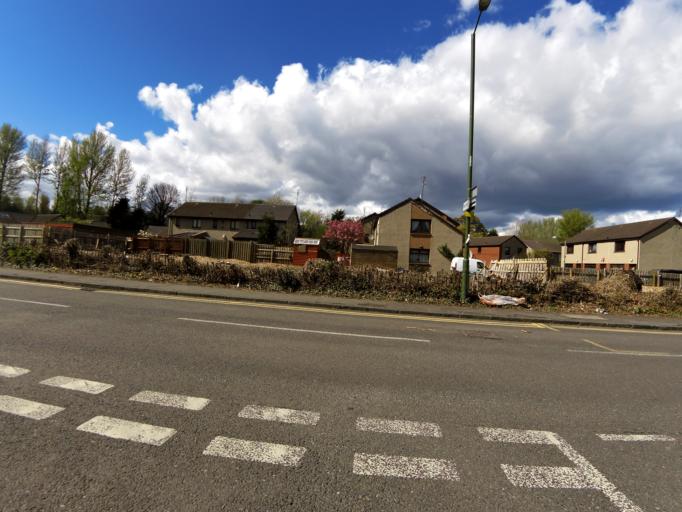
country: GB
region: Scotland
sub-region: Midlothian
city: Loanhead
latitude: 55.9185
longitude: -3.1393
